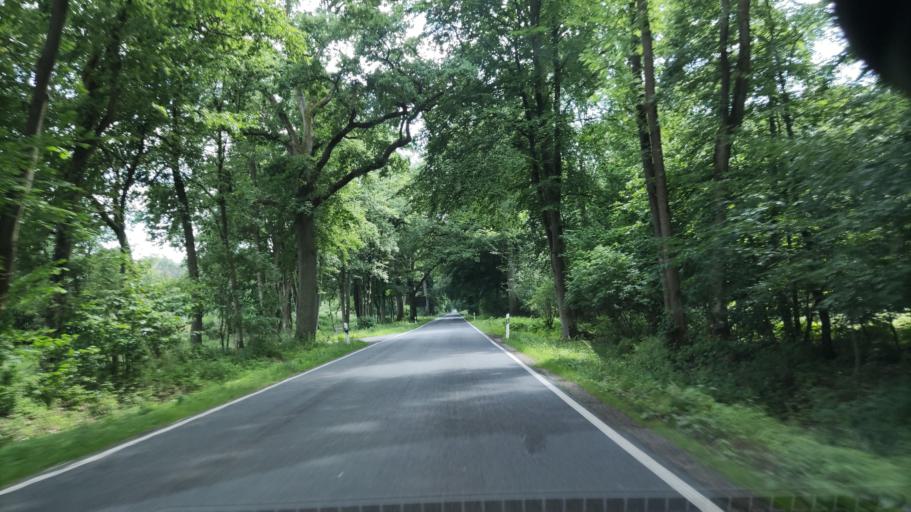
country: DE
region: Mecklenburg-Vorpommern
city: Lubtheen
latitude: 53.3551
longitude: 11.1437
